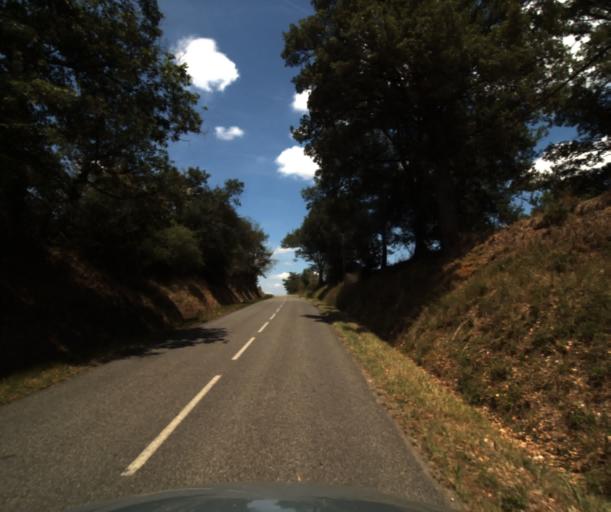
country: FR
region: Midi-Pyrenees
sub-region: Departement de la Haute-Garonne
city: Saint-Lys
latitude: 43.4865
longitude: 1.1821
